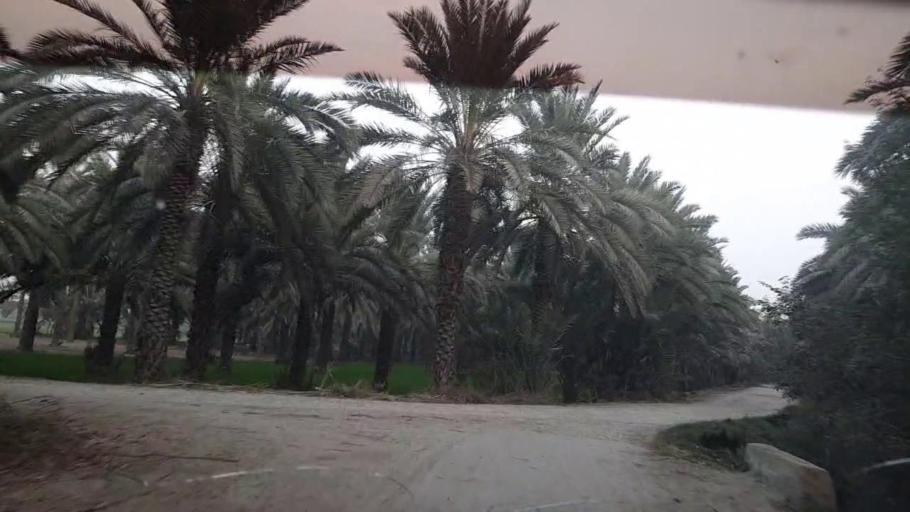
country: PK
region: Sindh
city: Khairpur
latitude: 27.5805
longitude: 68.7408
